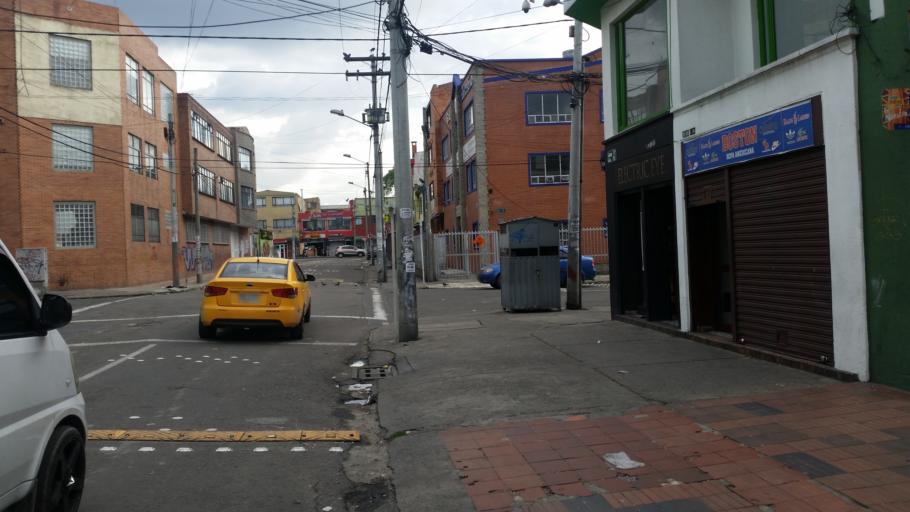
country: CO
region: Bogota D.C.
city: Bogota
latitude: 4.6451
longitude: -74.0664
